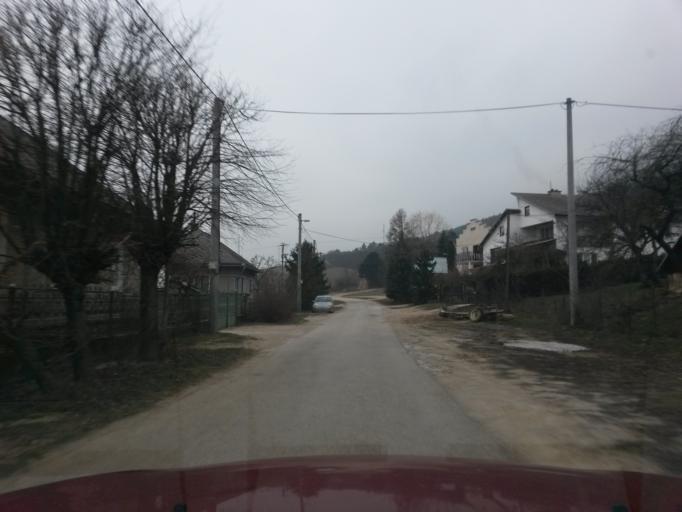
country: SK
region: Kosicky
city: Medzev
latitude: 48.6033
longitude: 20.7418
